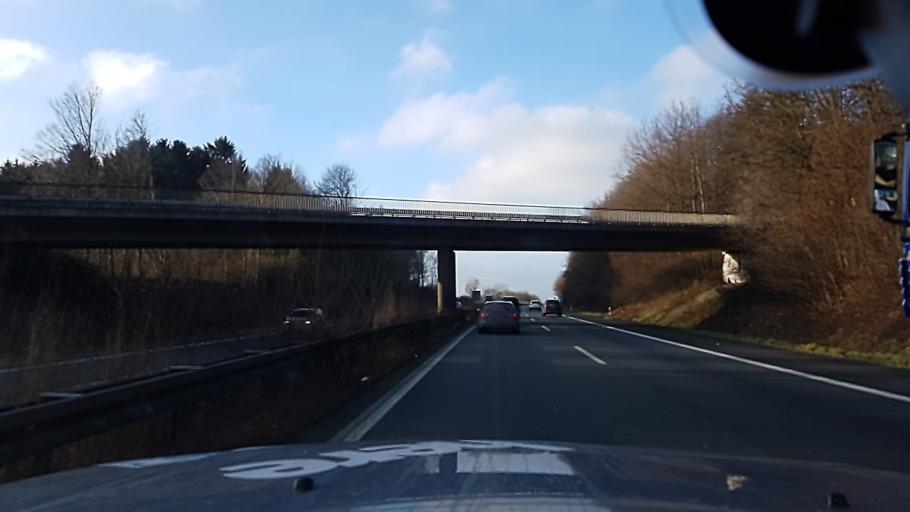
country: DE
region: North Rhine-Westphalia
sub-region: Regierungsbezirk Munster
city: Tecklenburg
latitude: 52.2531
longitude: 7.7872
